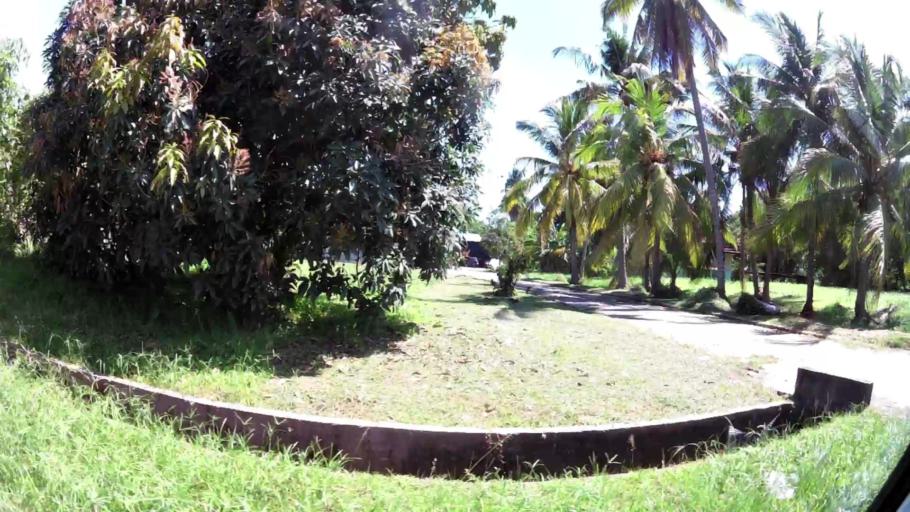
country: BN
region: Brunei and Muara
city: Bandar Seri Begawan
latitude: 4.9410
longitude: 114.9481
